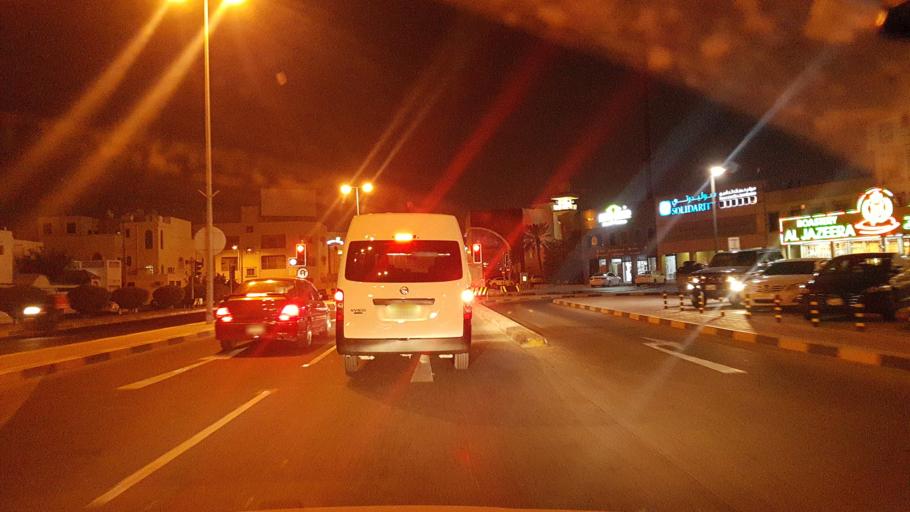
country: BH
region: Muharraq
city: Al Muharraq
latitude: 26.2578
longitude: 50.6290
